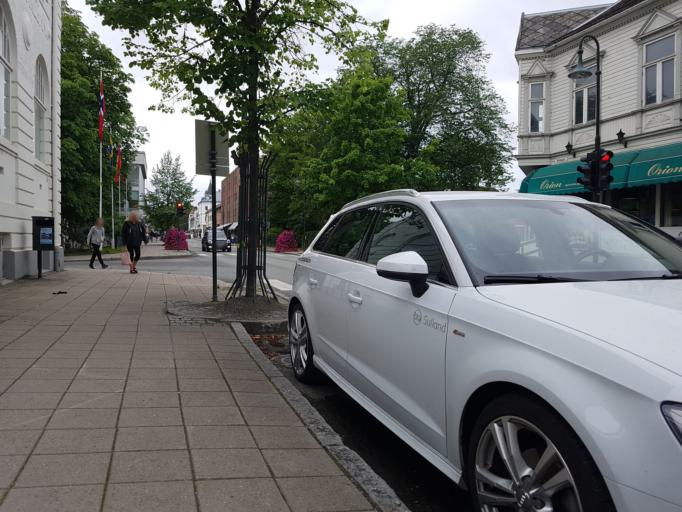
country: NO
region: Nord-Trondelag
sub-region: Levanger
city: Levanger
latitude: 63.7471
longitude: 11.2999
